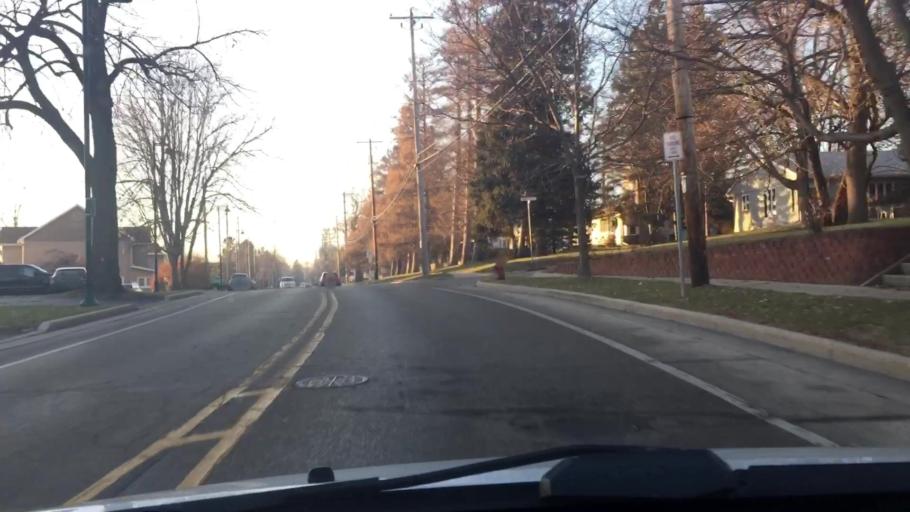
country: US
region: Wisconsin
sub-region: Waukesha County
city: Pewaukee
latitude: 43.0864
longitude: -88.2671
